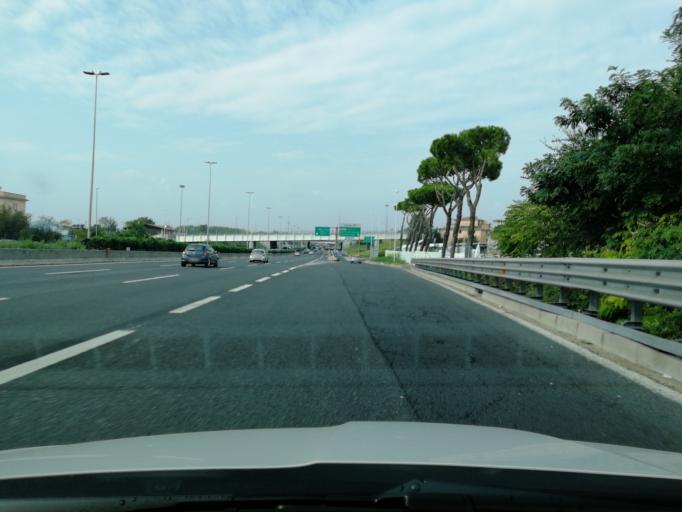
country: IT
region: Latium
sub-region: Citta metropolitana di Roma Capitale
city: Setteville
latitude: 41.9174
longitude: 12.6140
